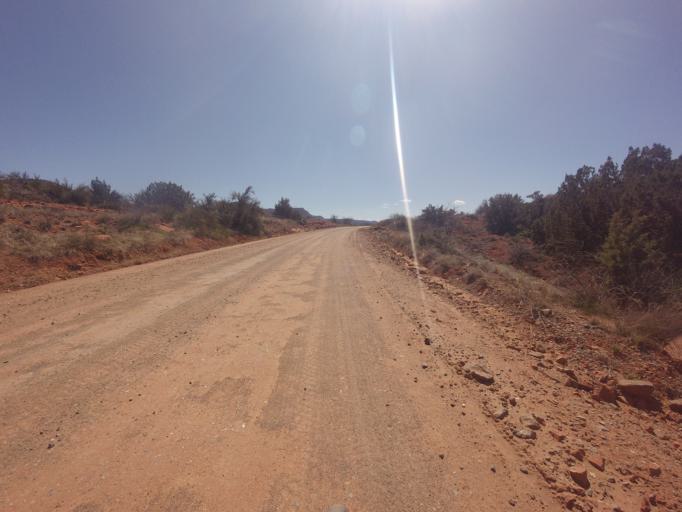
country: US
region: Arizona
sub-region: Yavapai County
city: Lake Montezuma
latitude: 34.6622
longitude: -111.7135
